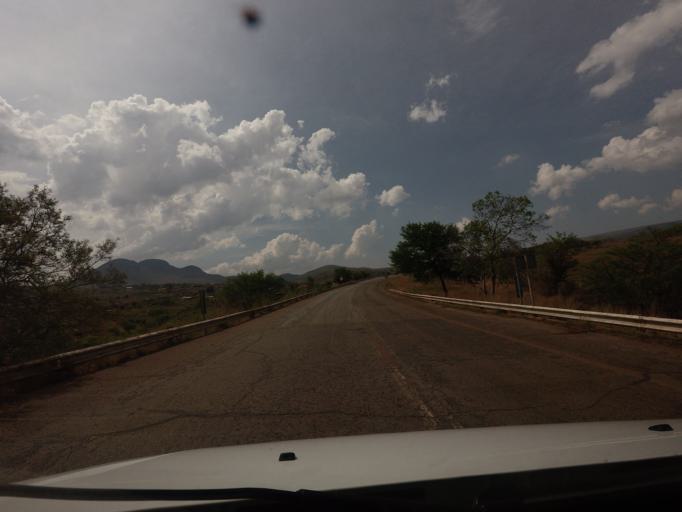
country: ZA
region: Mpumalanga
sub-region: Ehlanzeni District
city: Graksop
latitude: -24.6766
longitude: 30.8039
